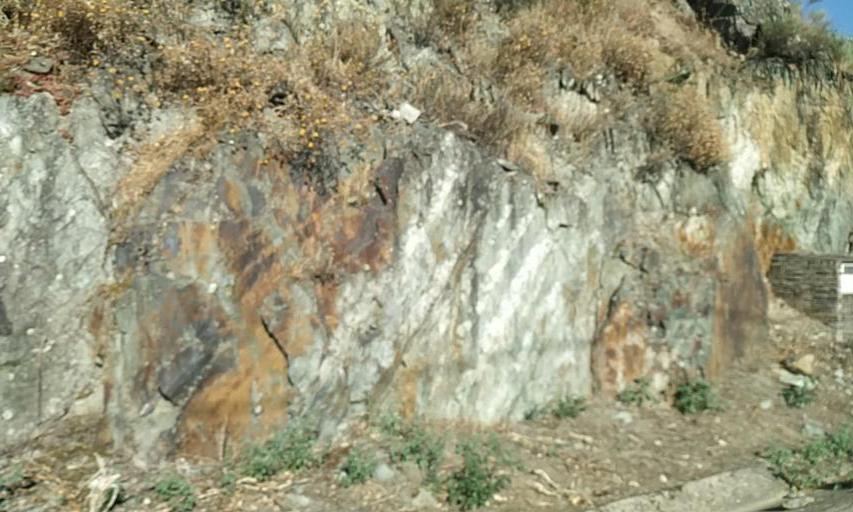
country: PT
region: Viseu
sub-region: Sao Joao da Pesqueira
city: Sao Joao da Pesqueira
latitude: 41.1818
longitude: -7.4394
